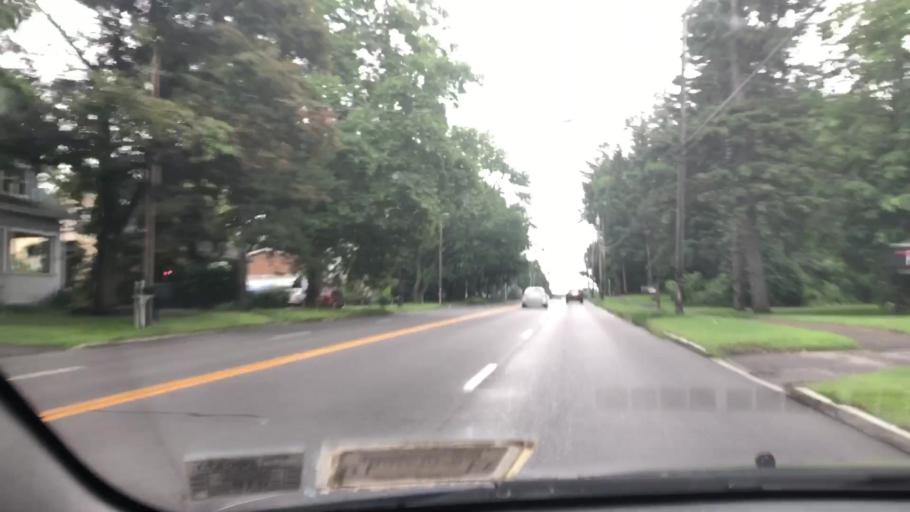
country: US
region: New York
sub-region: Monroe County
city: East Rochester
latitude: 43.1055
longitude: -77.4910
